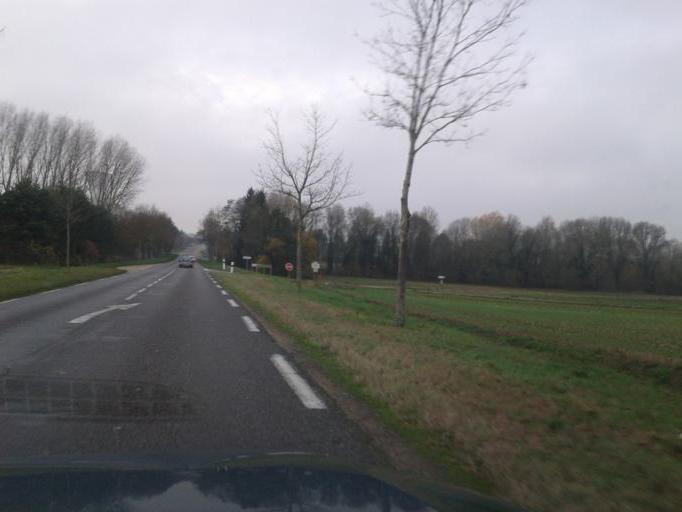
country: FR
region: Centre
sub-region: Departement du Loiret
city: Lailly-en-Val
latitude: 47.7798
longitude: 1.7027
